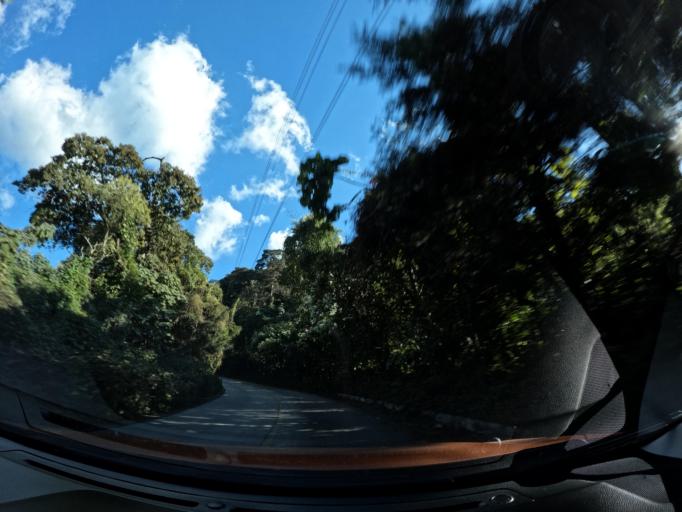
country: GT
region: Sacatepequez
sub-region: Municipio de Santa Maria de Jesus
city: Santa Maria de Jesus
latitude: 14.5129
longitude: -90.7219
